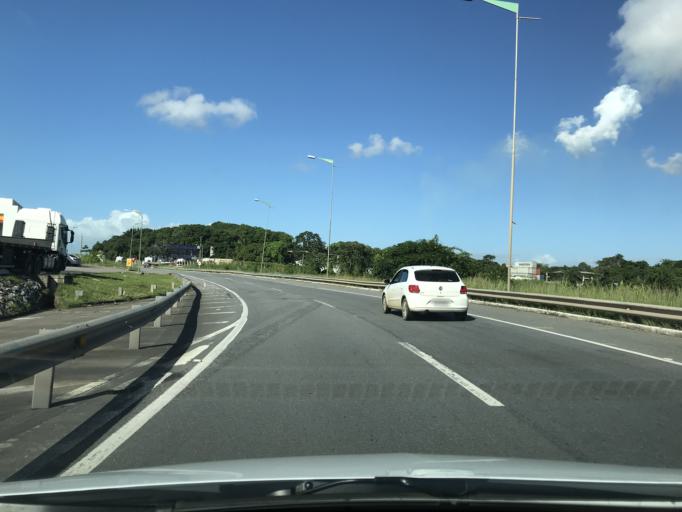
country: BR
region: Pernambuco
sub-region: Ipojuca
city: Ipojuca
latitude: -8.3674
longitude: -35.0086
